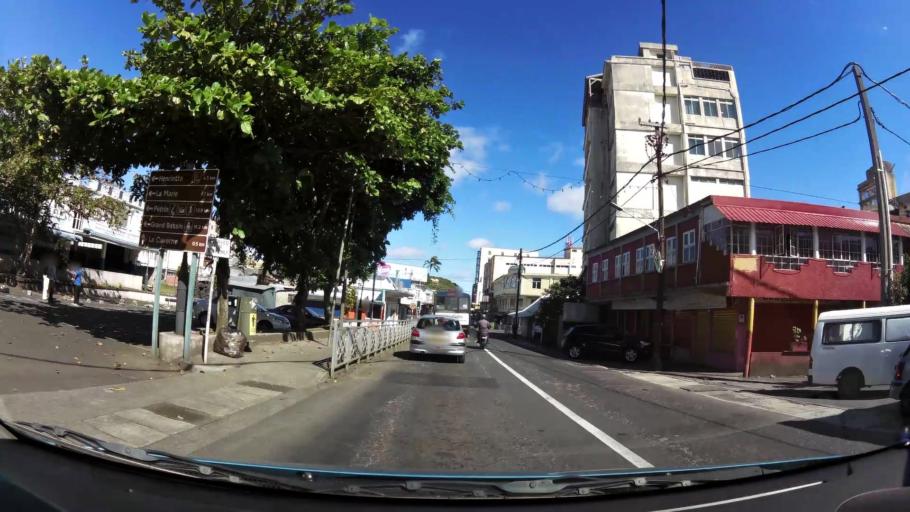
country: MU
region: Plaines Wilhems
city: Vacoas
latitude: -20.2986
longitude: 57.4934
